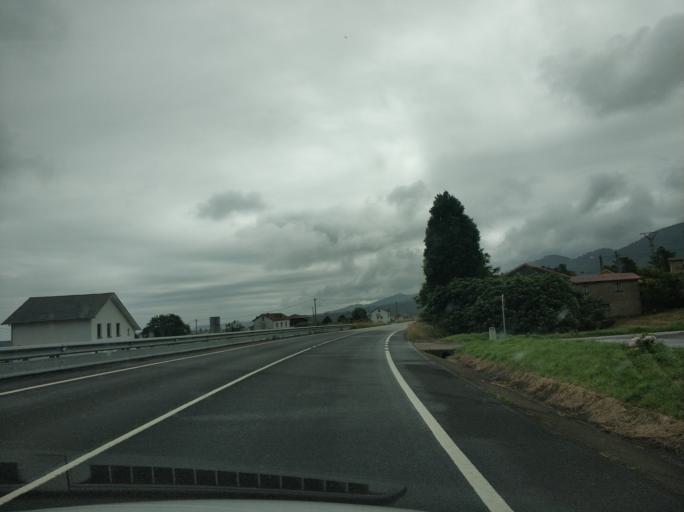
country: ES
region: Asturias
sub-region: Province of Asturias
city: Salas
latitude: 43.5450
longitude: -6.4020
